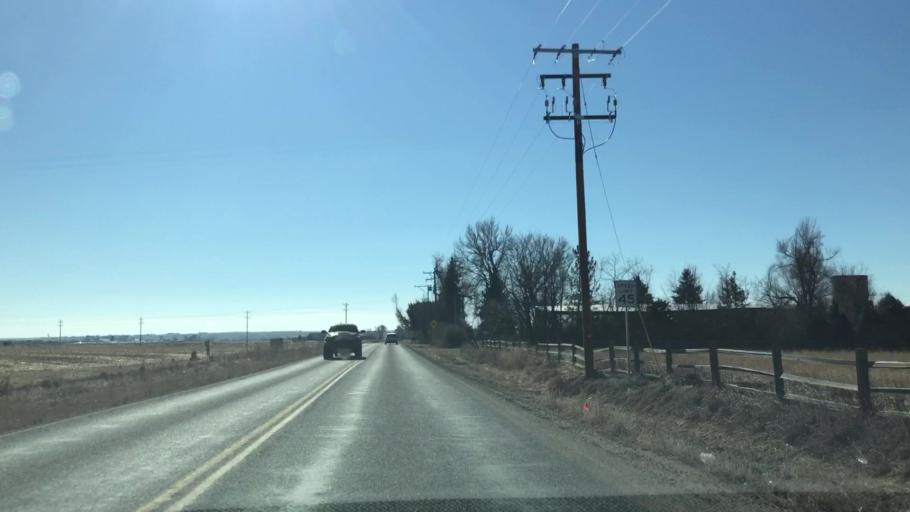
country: US
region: Colorado
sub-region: Weld County
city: Windsor
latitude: 40.5076
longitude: -104.9442
